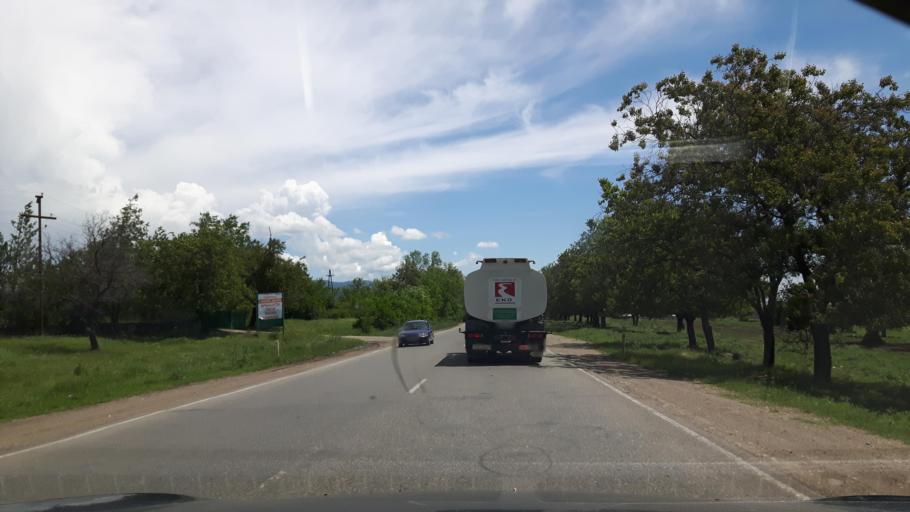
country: GE
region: Kakheti
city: Sagarejo
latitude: 41.7121
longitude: 45.1541
